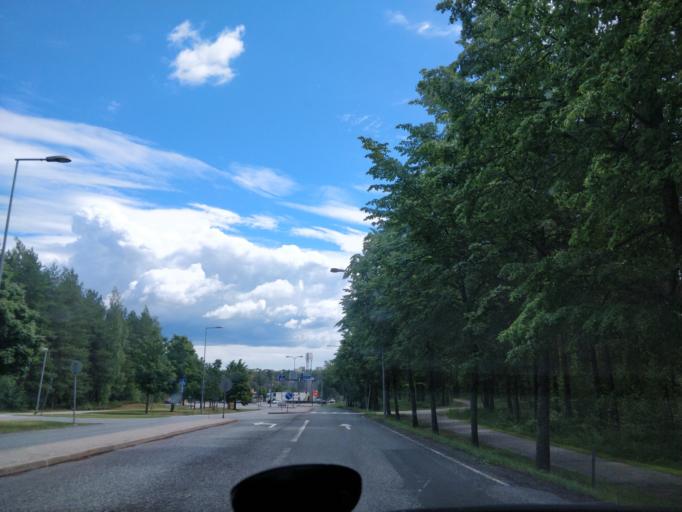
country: FI
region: Uusimaa
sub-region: Helsinki
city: Vantaa
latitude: 60.2828
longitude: 25.0760
